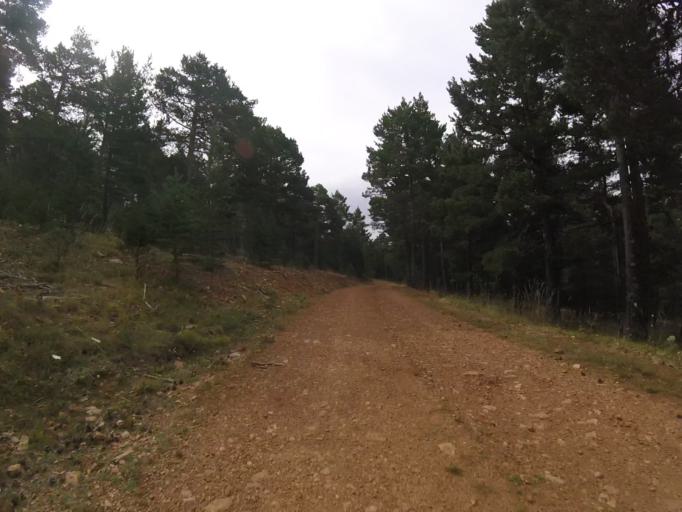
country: ES
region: Aragon
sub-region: Provincia de Teruel
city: Valdelinares
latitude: 40.3533
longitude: -0.5981
